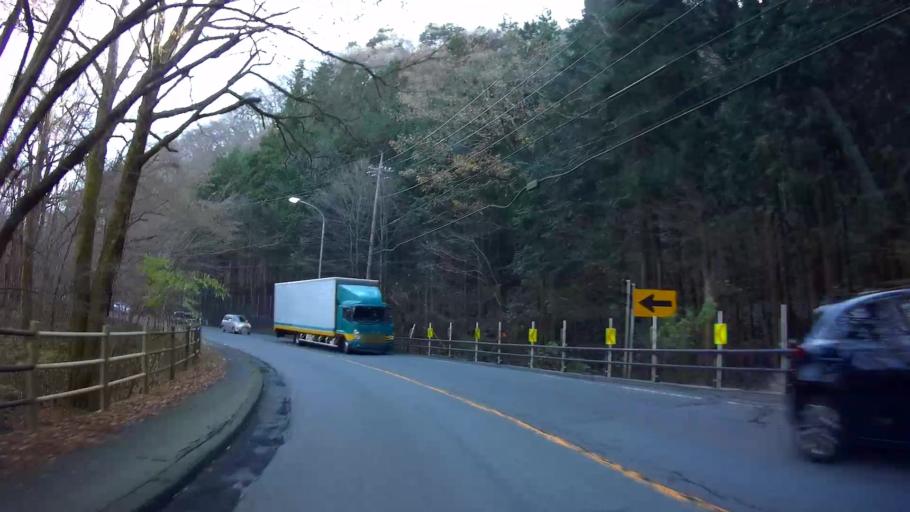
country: JP
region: Yamanashi
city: Fujikawaguchiko
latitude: 35.4743
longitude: 138.6076
